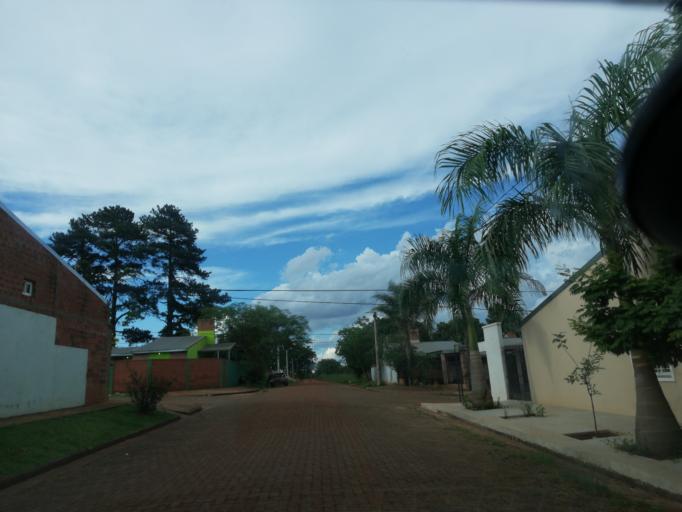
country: AR
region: Misiones
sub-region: Departamento de Capital
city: Posadas
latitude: -27.4193
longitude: -55.9231
